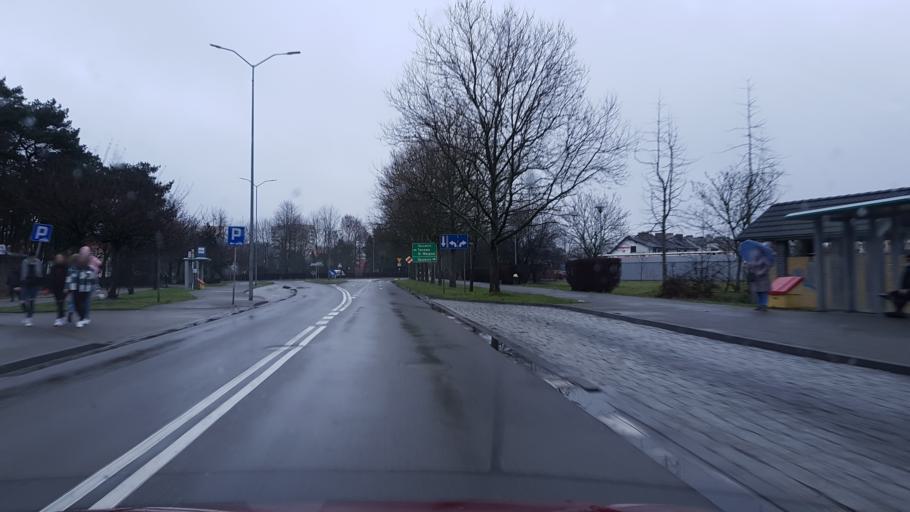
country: PL
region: West Pomeranian Voivodeship
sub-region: Powiat policki
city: Police
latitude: 53.5422
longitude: 14.5498
